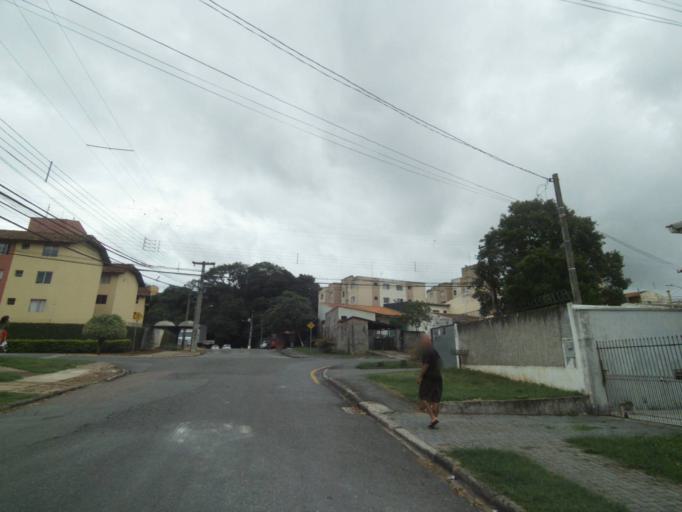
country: BR
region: Parana
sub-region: Curitiba
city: Curitiba
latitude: -25.4586
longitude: -49.3231
